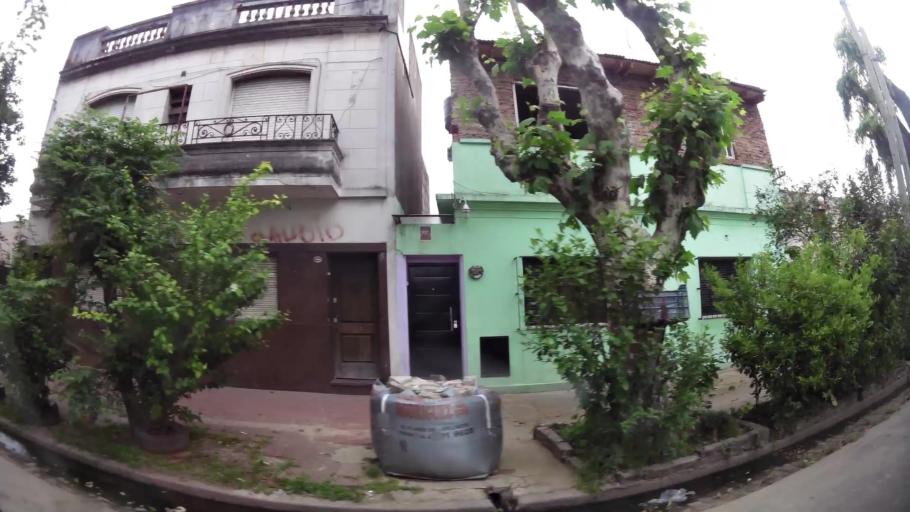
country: AR
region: Buenos Aires
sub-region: Partido de Avellaneda
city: Avellaneda
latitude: -34.6551
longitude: -58.3571
